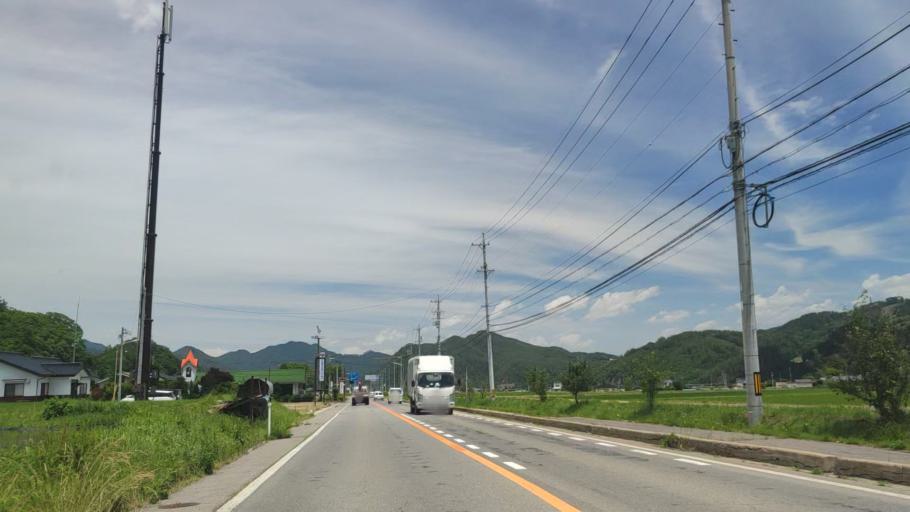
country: JP
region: Nagano
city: Kamimaruko
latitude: 36.2709
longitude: 138.2587
